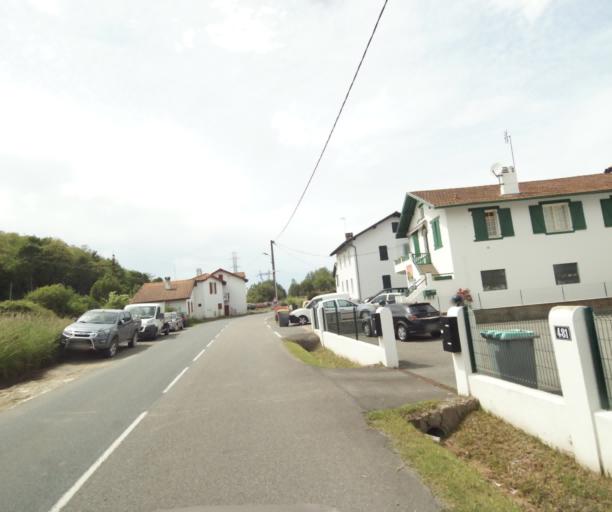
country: FR
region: Aquitaine
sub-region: Departement des Pyrenees-Atlantiques
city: Mouguerre
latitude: 43.4845
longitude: -1.4354
